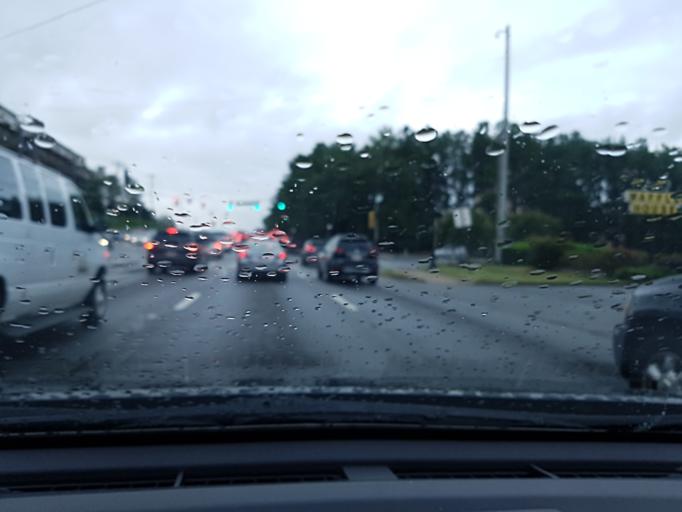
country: US
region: Georgia
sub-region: Gwinnett County
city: Duluth
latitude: 33.9501
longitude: -84.1287
